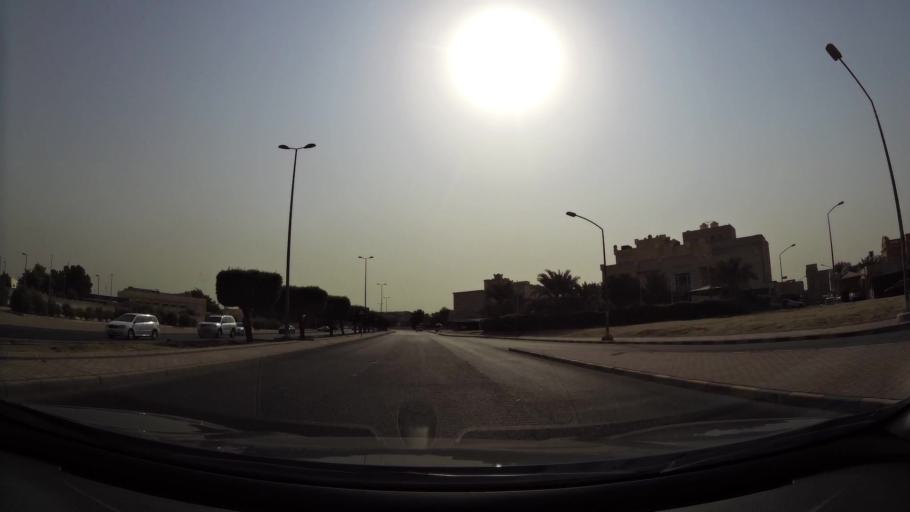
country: KW
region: Mubarak al Kabir
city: Sabah as Salim
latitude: 29.2594
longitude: 48.0639
